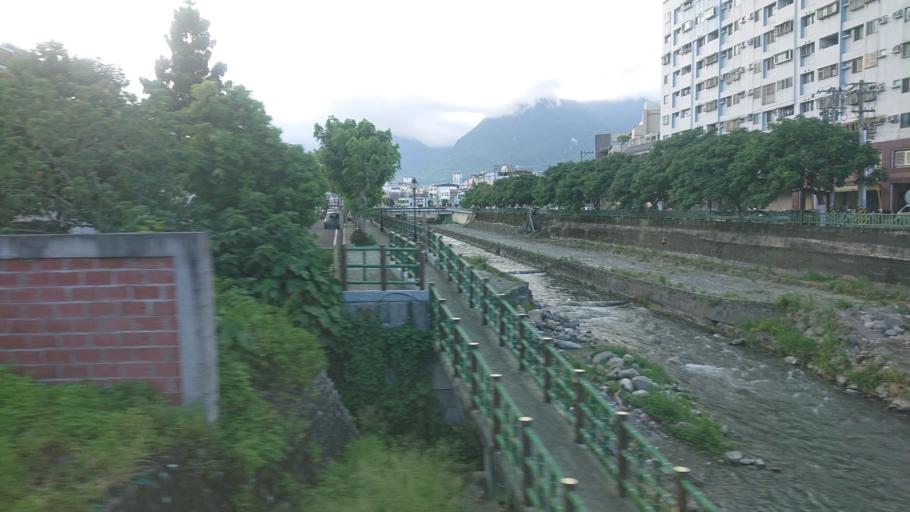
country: TW
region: Taiwan
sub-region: Hualien
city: Hualian
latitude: 23.9726
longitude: 121.5897
